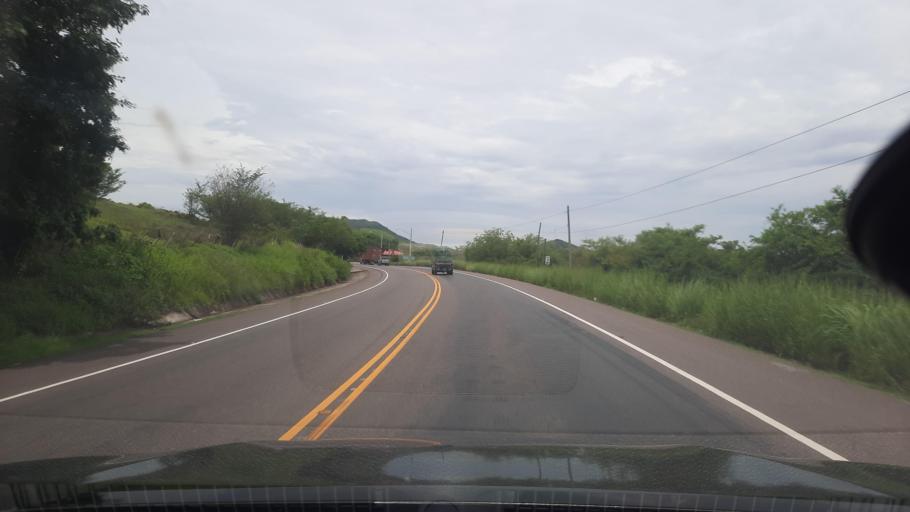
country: HN
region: Valle
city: Goascoran
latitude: 13.5517
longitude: -87.6469
